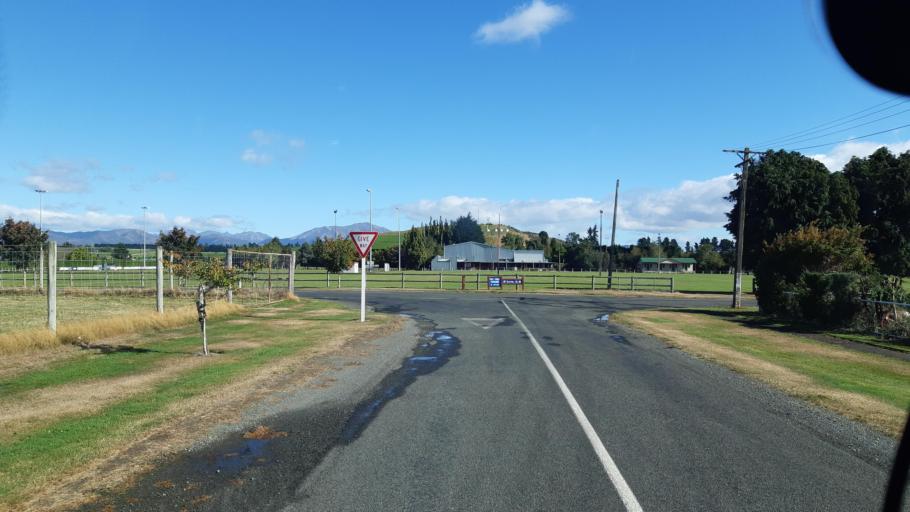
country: NZ
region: Southland
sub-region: Southland District
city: Winton
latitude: -45.6700
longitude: 168.2365
